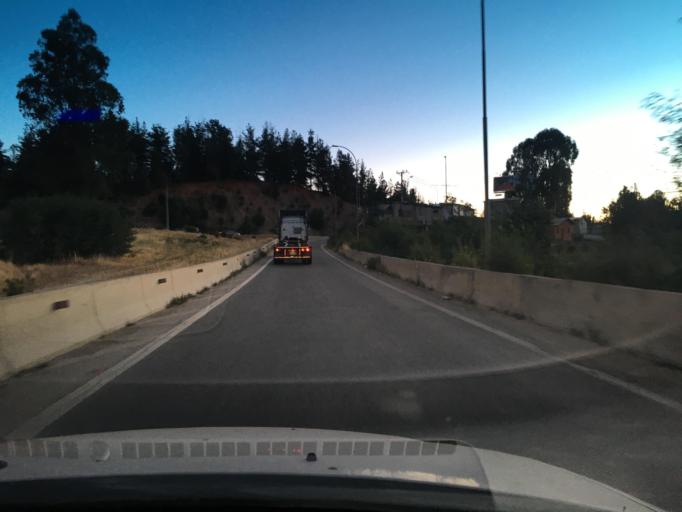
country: CL
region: Valparaiso
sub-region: Provincia de Valparaiso
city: Vina del Mar
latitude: -33.1080
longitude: -71.5569
